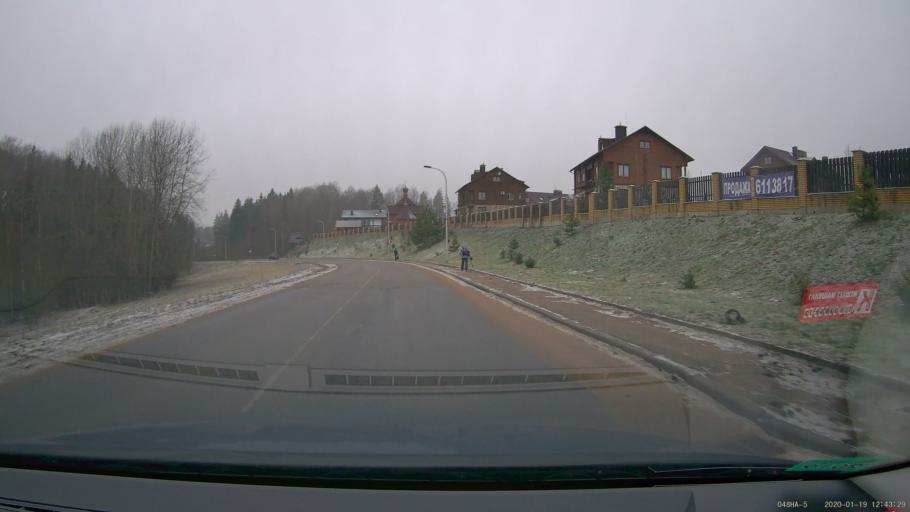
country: BY
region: Minsk
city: Lahoysk
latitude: 54.1775
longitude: 27.8157
